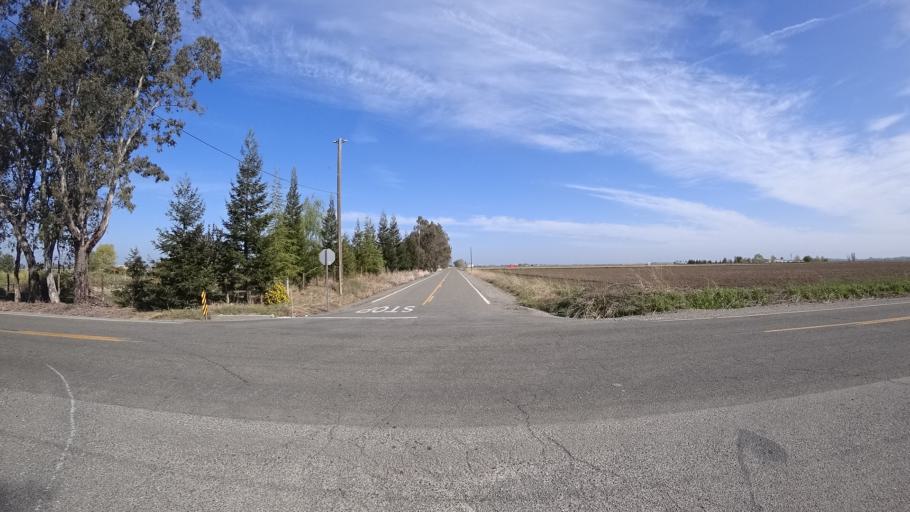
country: US
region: California
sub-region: Glenn County
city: Hamilton City
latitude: 39.5824
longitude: -122.0370
